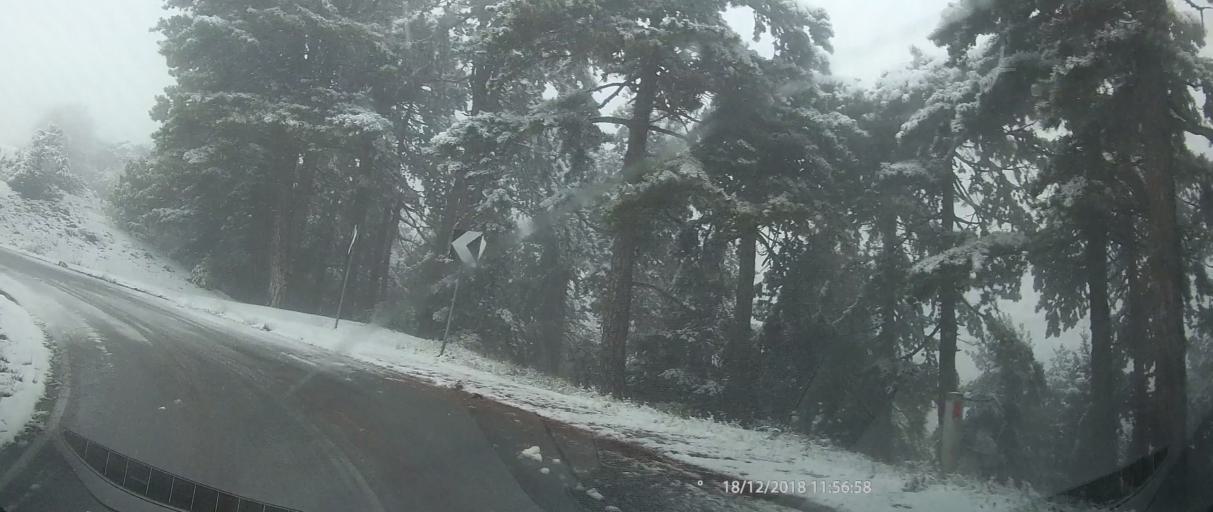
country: GR
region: Central Macedonia
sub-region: Nomos Pierias
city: Litochoro
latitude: 40.1130
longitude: 22.4695
